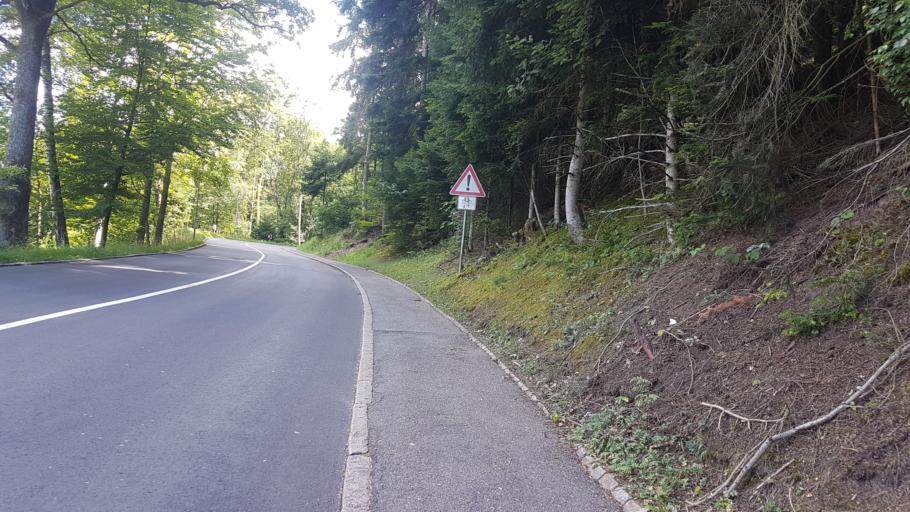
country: DE
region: Baden-Wuerttemberg
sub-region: Freiburg Region
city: Schramberg
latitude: 48.2289
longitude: 8.4005
